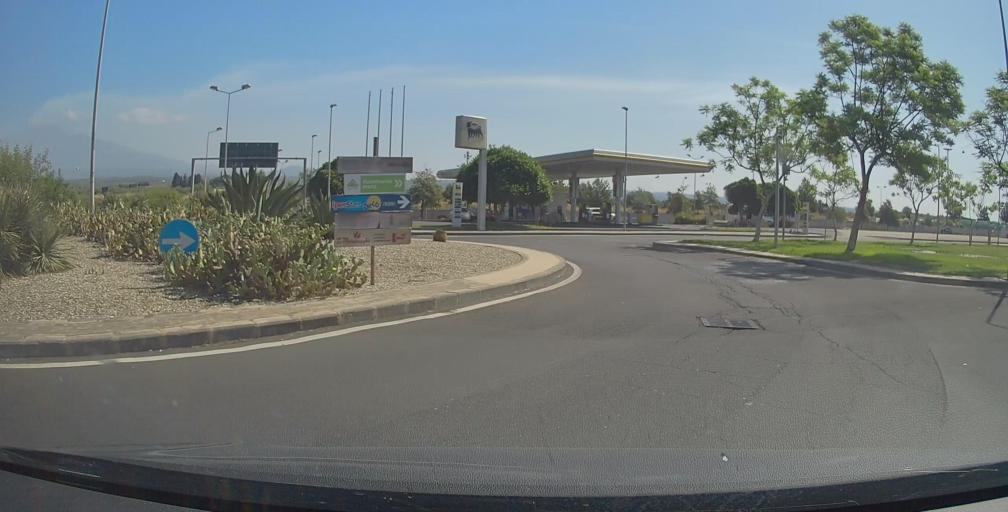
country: IT
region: Sicily
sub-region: Catania
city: Palazzolo
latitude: 37.5480
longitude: 14.9477
